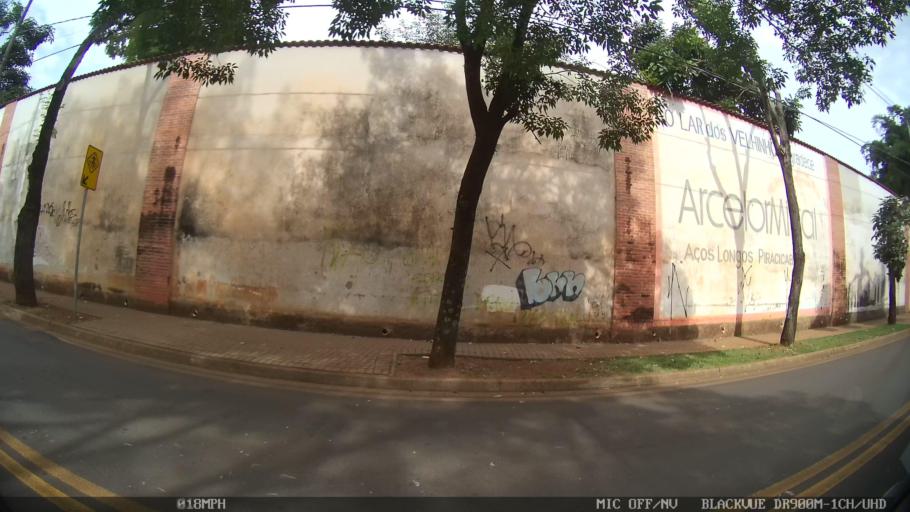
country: BR
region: Sao Paulo
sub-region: Piracicaba
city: Piracicaba
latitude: -22.7069
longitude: -47.6487
